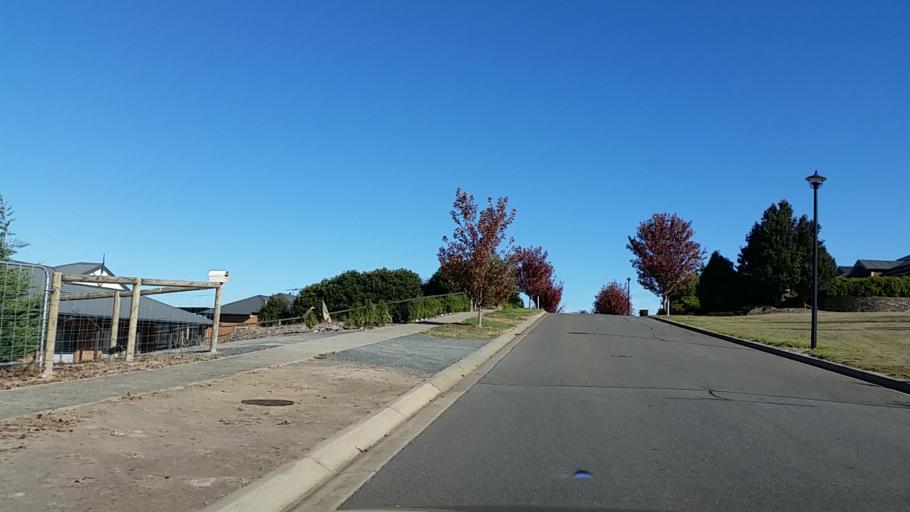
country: AU
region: South Australia
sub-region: Mount Barker
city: Mount Barker
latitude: -35.0596
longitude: 138.8858
